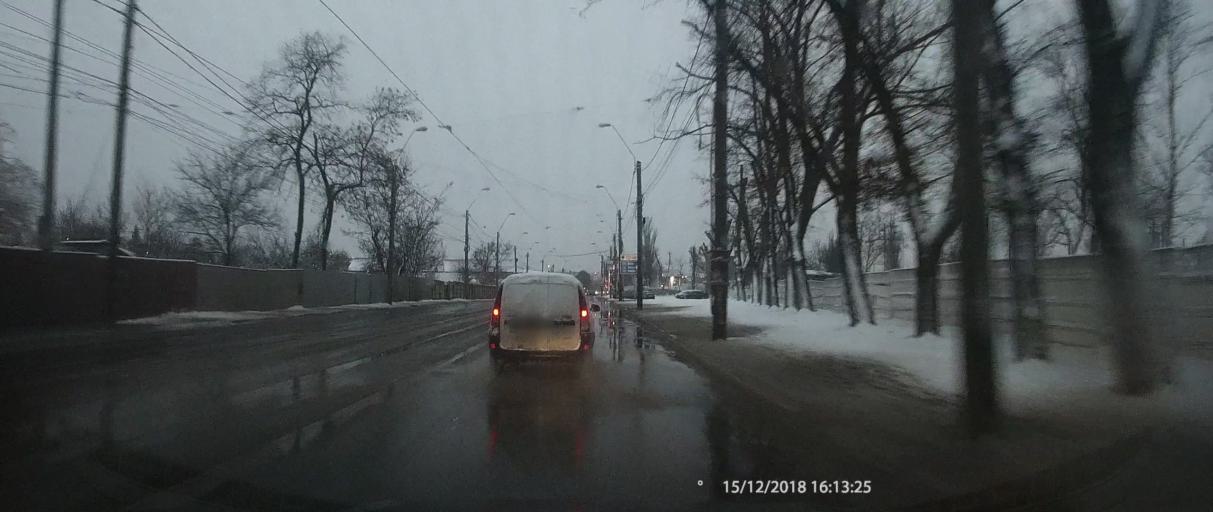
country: RO
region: Galati
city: Galati
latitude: 45.4635
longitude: 28.0336
